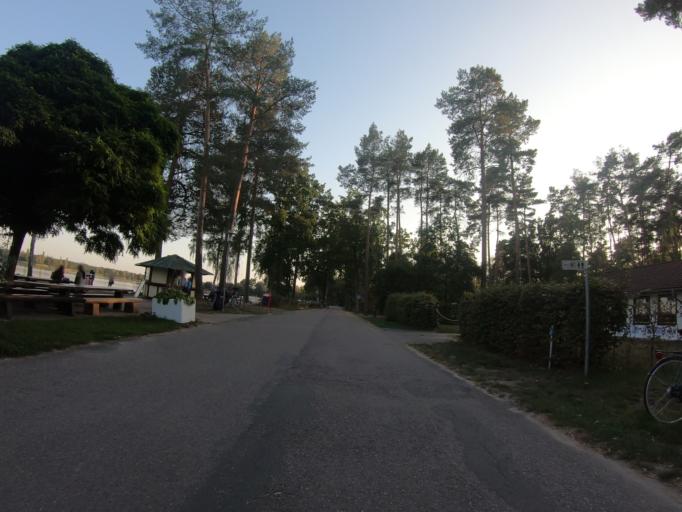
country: DE
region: Lower Saxony
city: Calberlah
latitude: 52.4562
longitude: 10.6183
